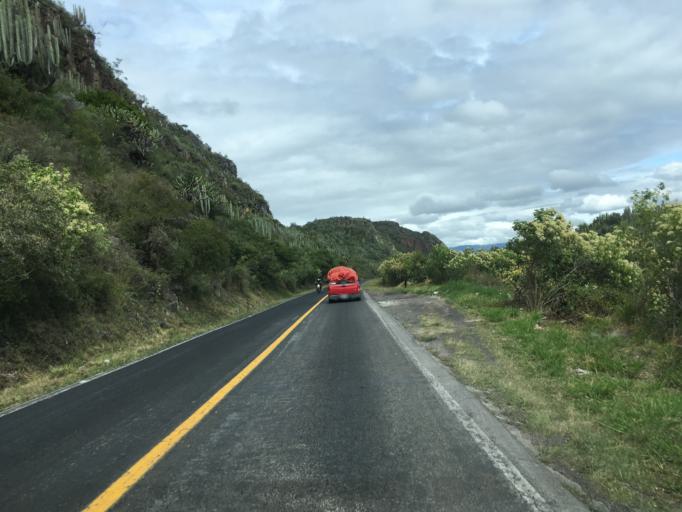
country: MX
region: Hidalgo
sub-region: Atotonilco el Grande
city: Santa Maria Amajac
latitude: 20.4212
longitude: -98.6874
